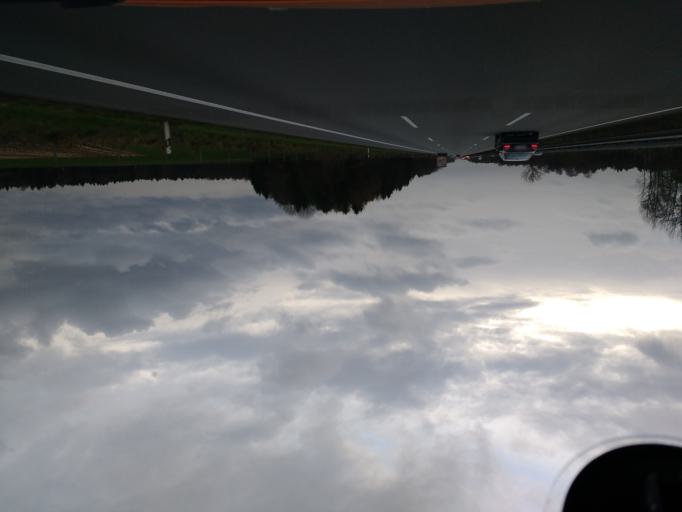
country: DE
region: Lower Saxony
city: Halvesbostel
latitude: 53.3247
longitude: 9.5912
